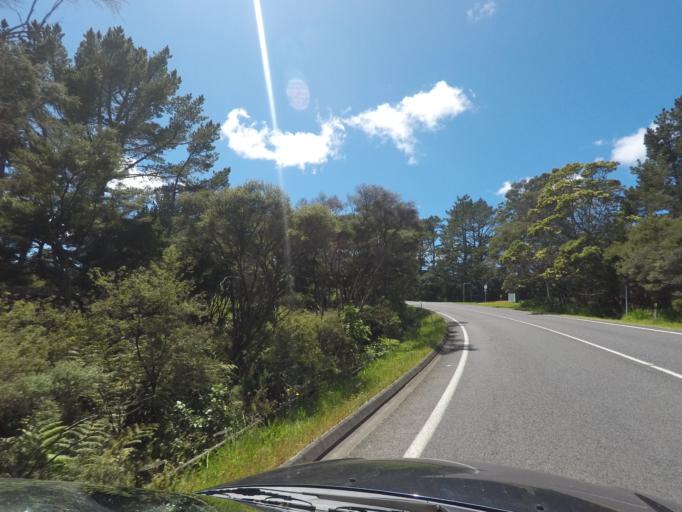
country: NZ
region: Auckland
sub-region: Auckland
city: Rothesay Bay
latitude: -36.7609
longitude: 174.6579
